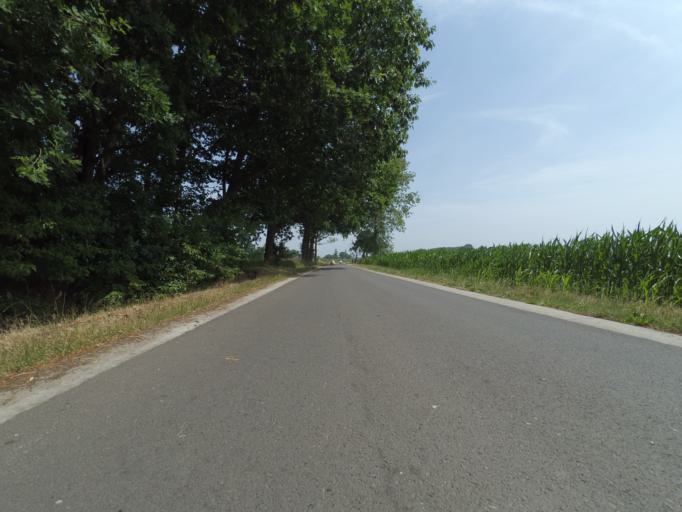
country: BE
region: Flanders
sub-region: Provincie Antwerpen
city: Essen
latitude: 51.4419
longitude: 4.4205
